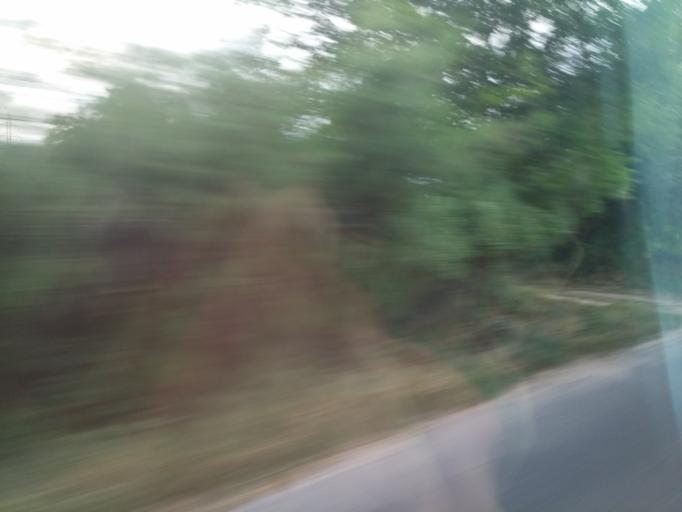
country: HU
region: Veszprem
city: Varpalota
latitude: 47.2130
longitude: 18.1511
